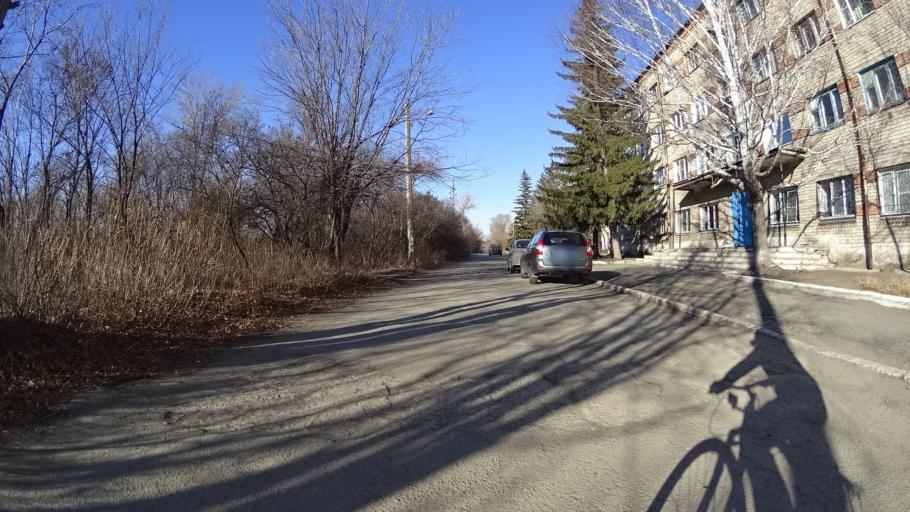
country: RU
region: Chelyabinsk
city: Troitsk
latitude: 54.0441
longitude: 61.6251
